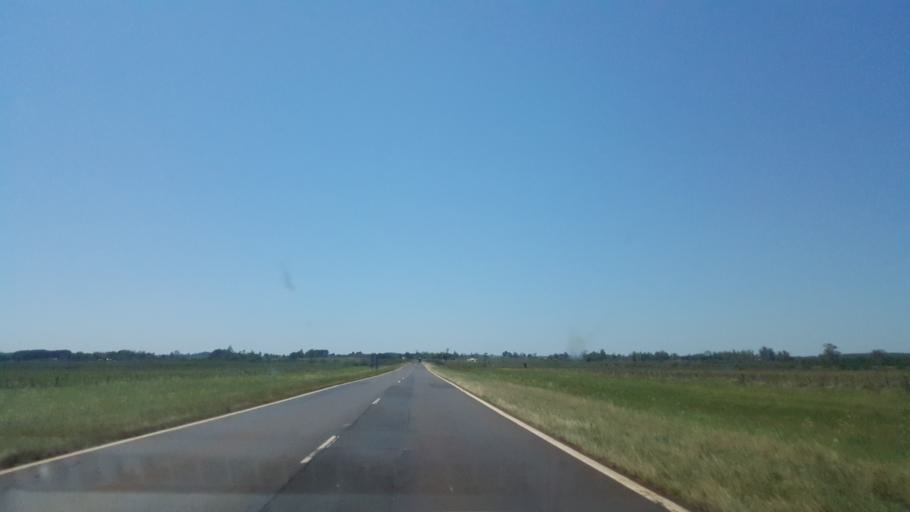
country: AR
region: Corrientes
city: Santo Tome
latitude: -28.5314
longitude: -56.1030
